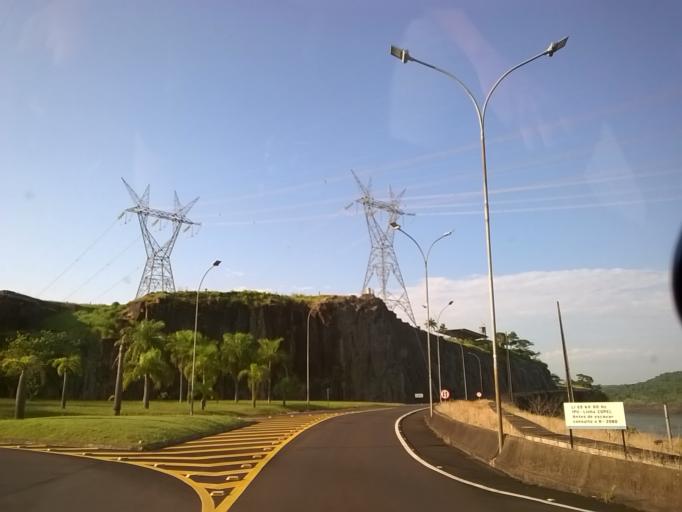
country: PY
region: Alto Parana
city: Ciudad del Este
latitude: -25.4111
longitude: -54.5850
